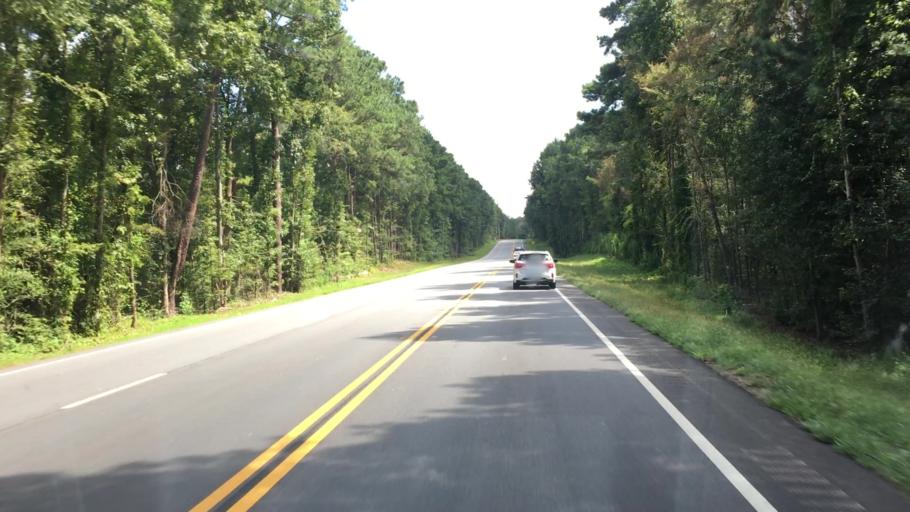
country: US
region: Georgia
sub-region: Putnam County
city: Jefferson
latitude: 33.4318
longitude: -83.3742
